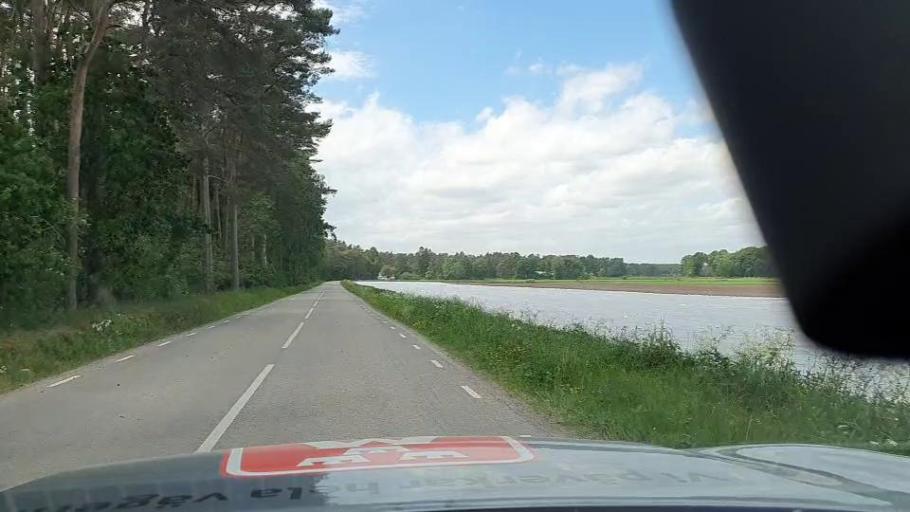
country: SE
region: Blekinge
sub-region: Karlshamns Kommun
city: Morrum
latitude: 56.0908
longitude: 14.7041
